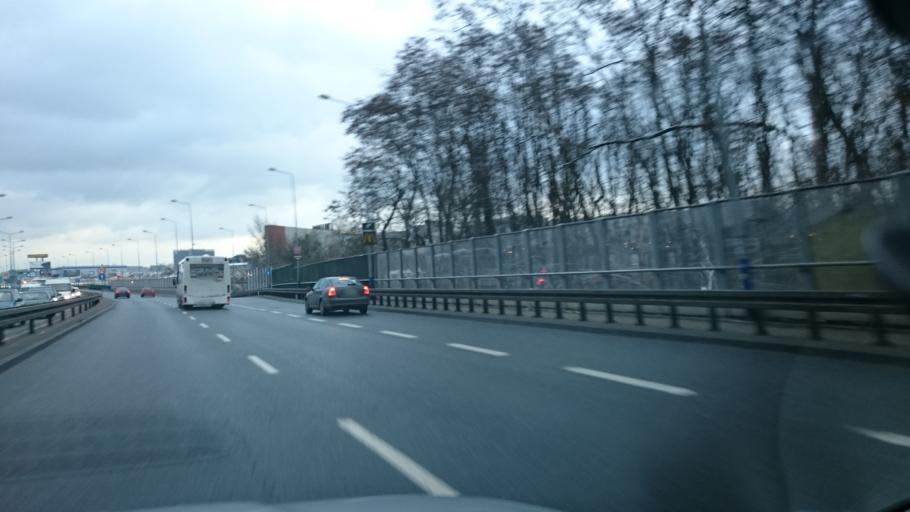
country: PL
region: Lesser Poland Voivodeship
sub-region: Krakow
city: Krakow
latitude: 50.0303
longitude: 19.9511
